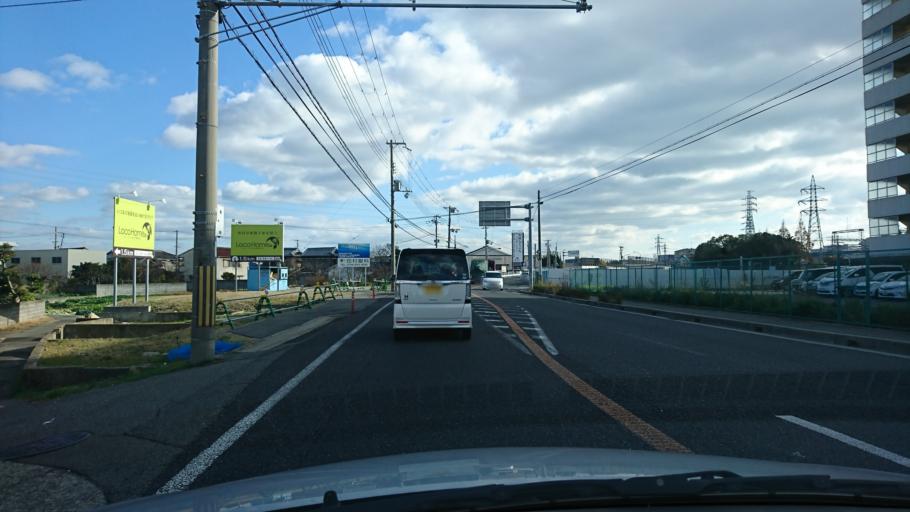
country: JP
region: Hyogo
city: Akashi
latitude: 34.6590
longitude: 134.9714
